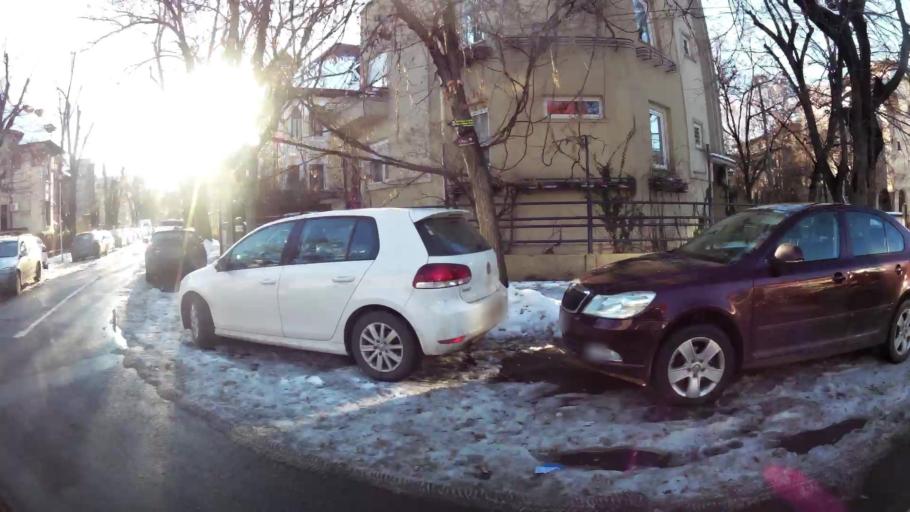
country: RO
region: Bucuresti
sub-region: Municipiul Bucuresti
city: Bucuresti
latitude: 44.4308
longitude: 26.0713
